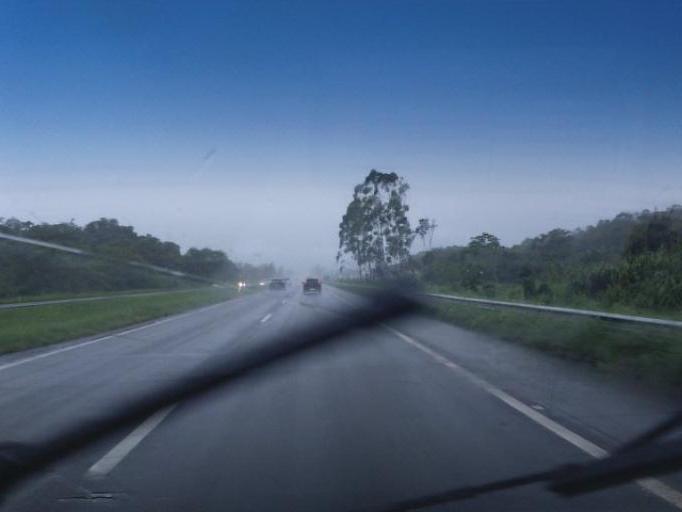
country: BR
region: Sao Paulo
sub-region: Miracatu
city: Miracatu
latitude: -24.2754
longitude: -47.4125
